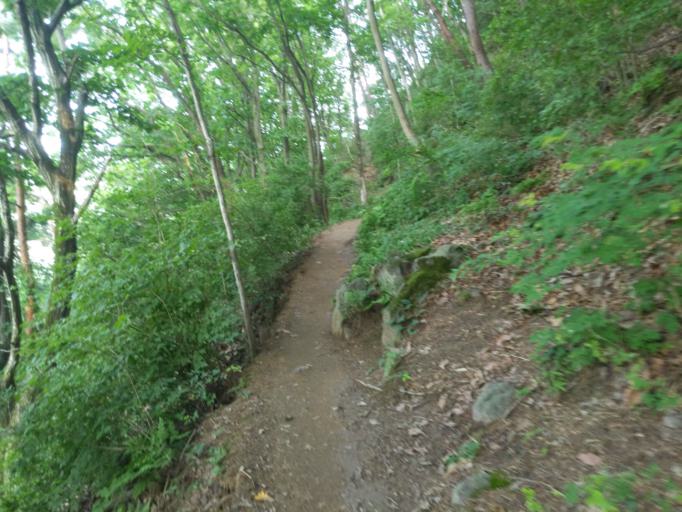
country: KR
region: Daegu
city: Hwawon
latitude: 35.7862
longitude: 128.5463
